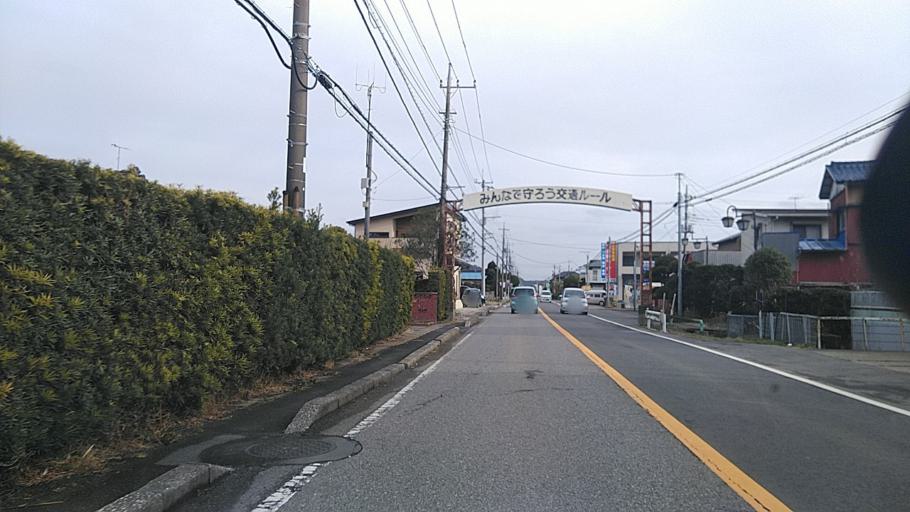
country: JP
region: Chiba
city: Togane
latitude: 35.5797
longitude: 140.3775
